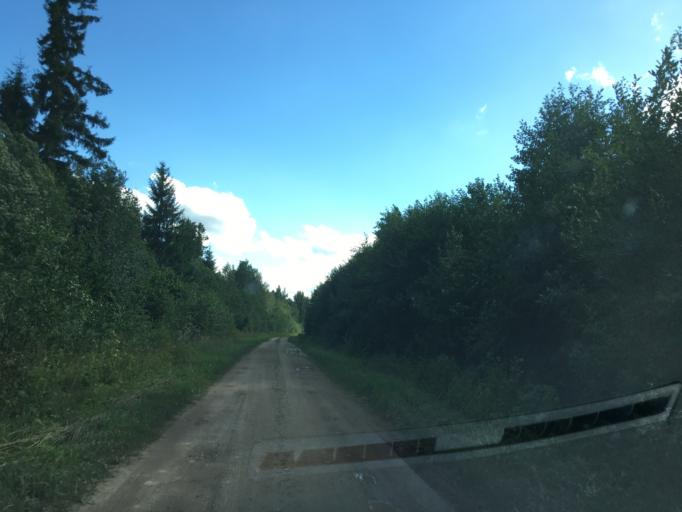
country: EE
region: Viljandimaa
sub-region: Suure-Jaani vald
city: Suure-Jaani
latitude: 58.4925
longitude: 25.2561
